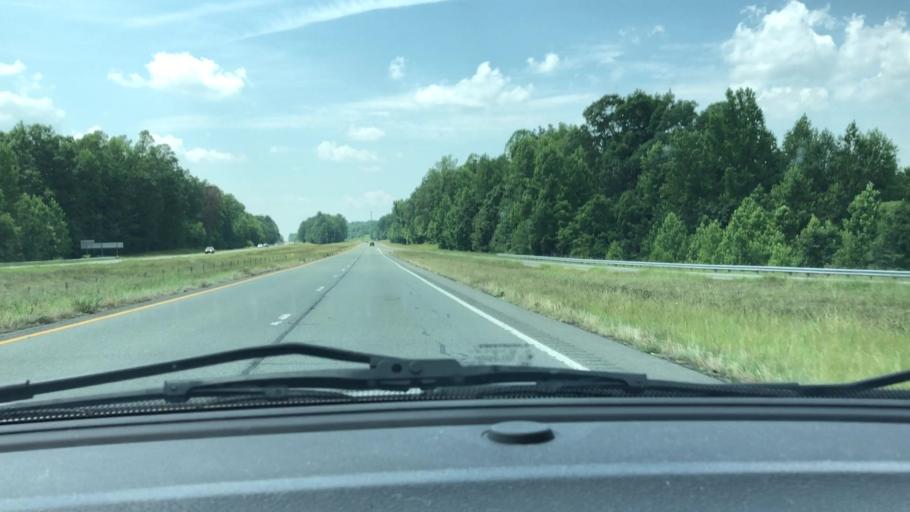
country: US
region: North Carolina
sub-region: Chatham County
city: Siler City
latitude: 35.7657
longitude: -79.4768
